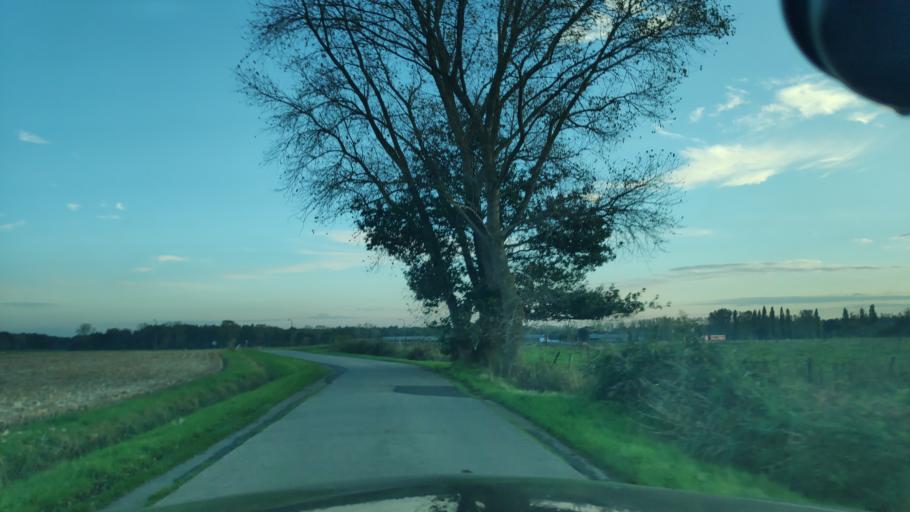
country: BE
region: Flanders
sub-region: Provincie Oost-Vlaanderen
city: Eeklo
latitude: 51.1470
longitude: 3.5033
